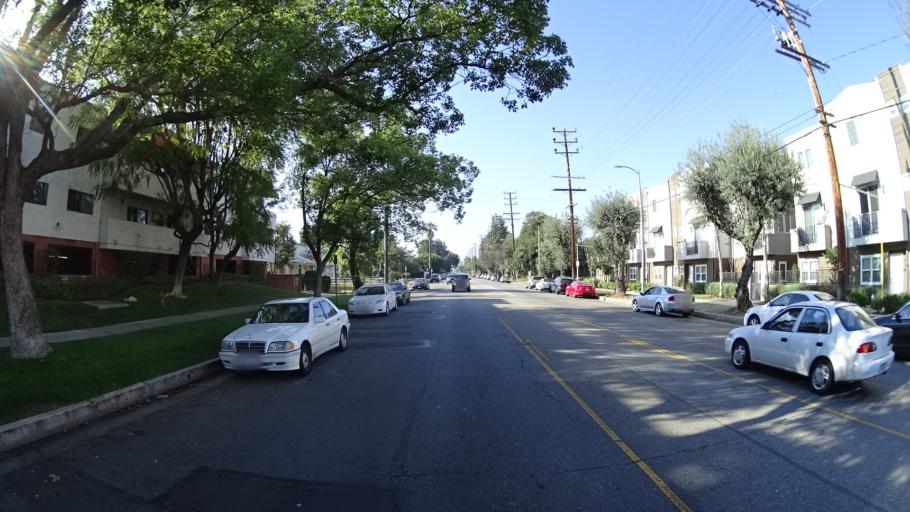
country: US
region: California
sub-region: Los Angeles County
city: Van Nuys
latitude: 34.1733
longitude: -118.4399
